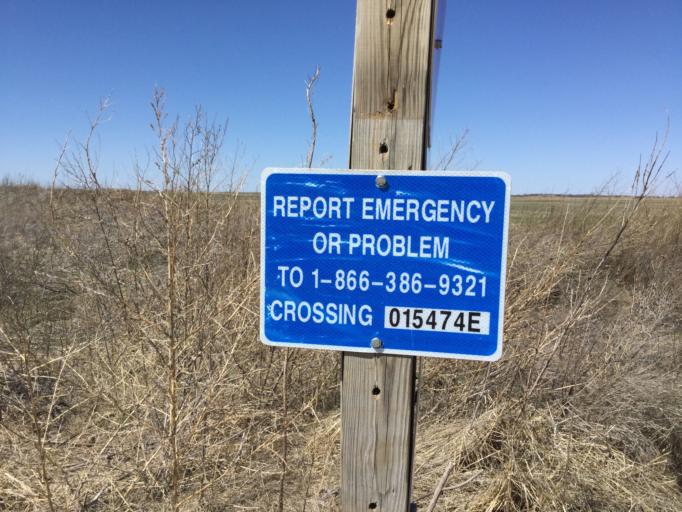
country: US
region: Kansas
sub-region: Barber County
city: Medicine Lodge
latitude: 37.4574
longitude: -98.5105
